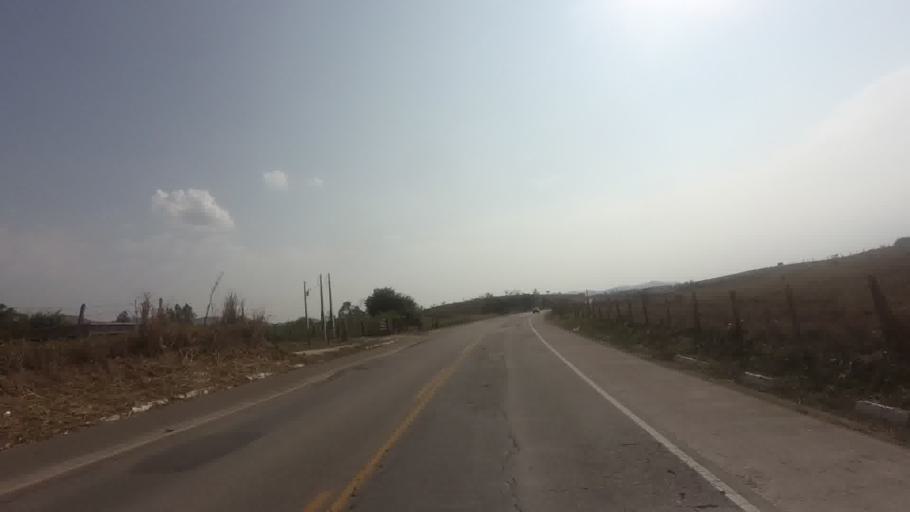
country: BR
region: Rio de Janeiro
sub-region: Bom Jesus Do Itabapoana
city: Bom Jesus do Itabapoana
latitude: -21.1528
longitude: -41.6030
